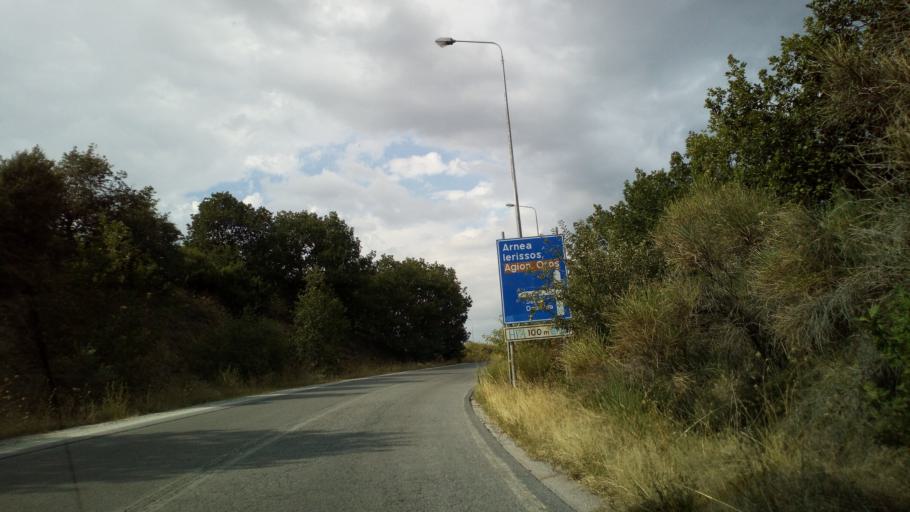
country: GR
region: Central Macedonia
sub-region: Nomos Chalkidikis
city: Polygyros
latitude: 40.4858
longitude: 23.4002
